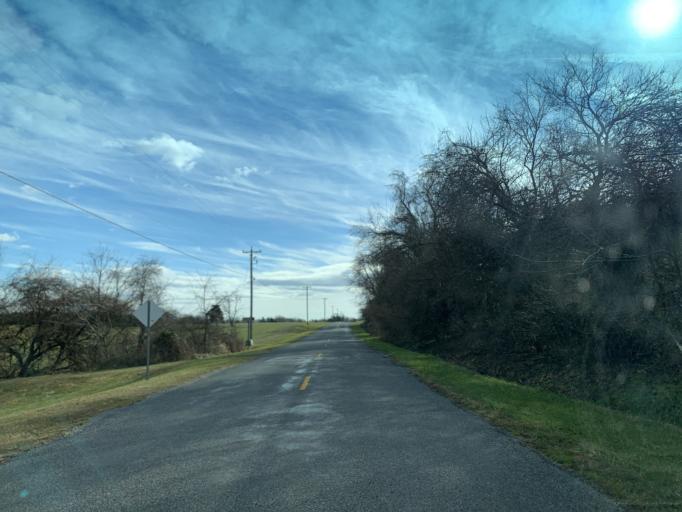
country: US
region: Maryland
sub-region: Kent County
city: Chestertown
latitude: 39.3372
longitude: -76.0480
